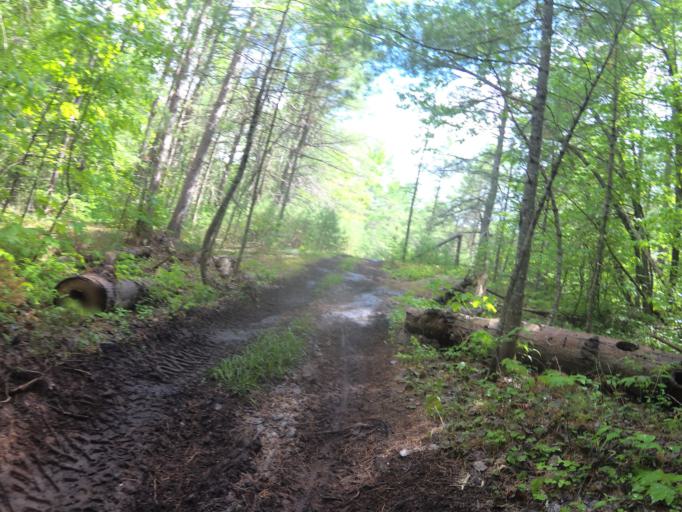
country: CA
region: Ontario
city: Renfrew
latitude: 45.1249
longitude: -76.8425
